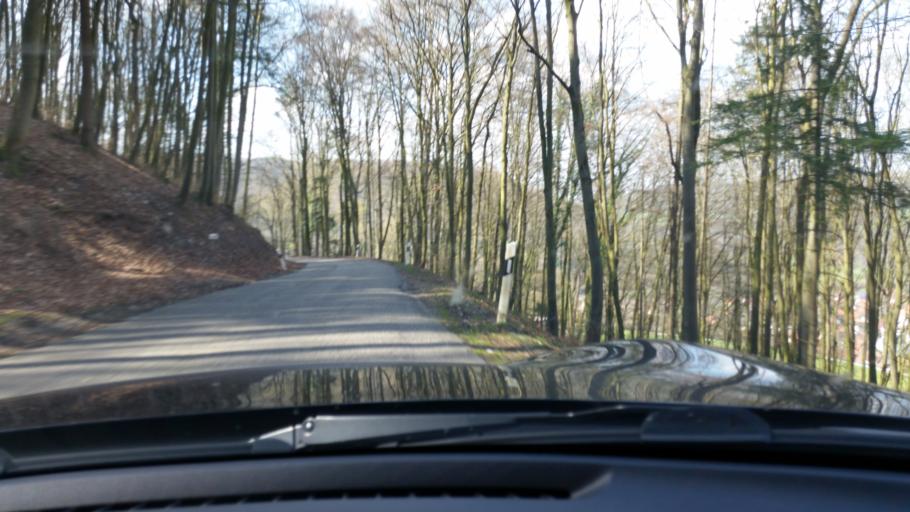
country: DE
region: Baden-Wuerttemberg
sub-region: Regierungsbezirk Stuttgart
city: Braunsbach
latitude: 49.2621
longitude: 9.7678
